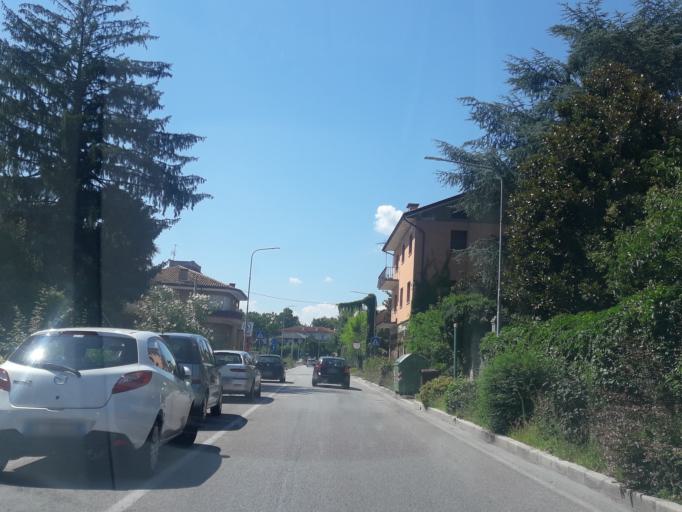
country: IT
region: Friuli Venezia Giulia
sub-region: Provincia di Udine
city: Udine
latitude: 46.0554
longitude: 13.2249
